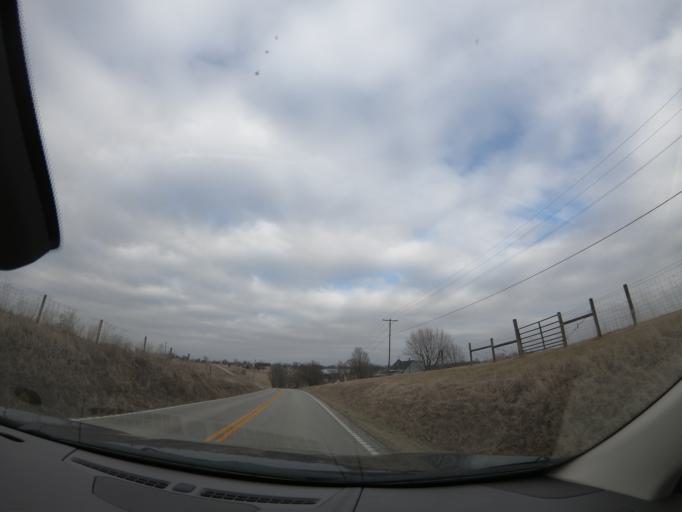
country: US
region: Kentucky
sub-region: Nelson County
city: Bardstown
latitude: 37.8535
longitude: -85.3445
